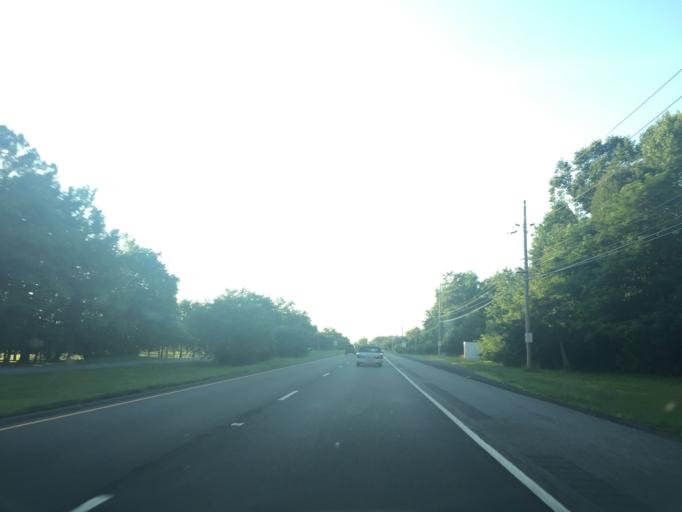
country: US
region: Delaware
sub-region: Kent County
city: Clayton
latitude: 39.3528
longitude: -75.6426
